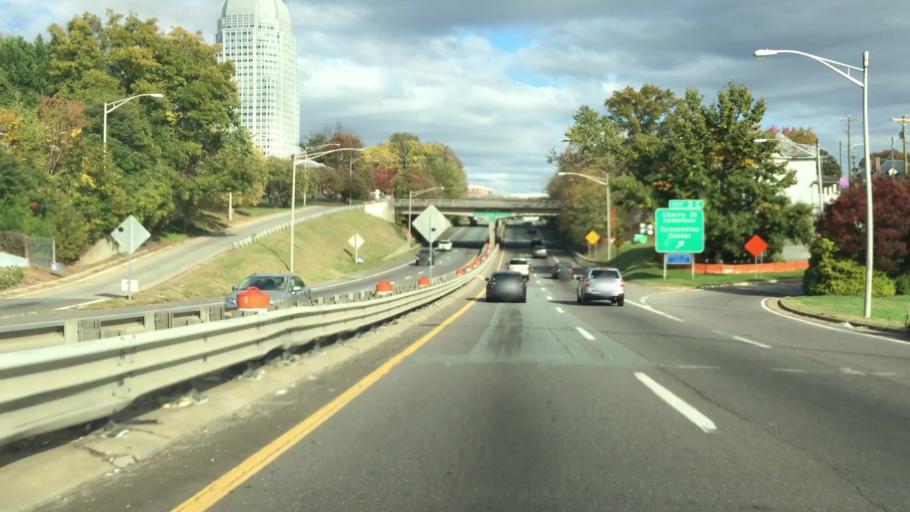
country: US
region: North Carolina
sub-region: Forsyth County
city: Winston-Salem
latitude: 36.0926
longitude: -80.2496
